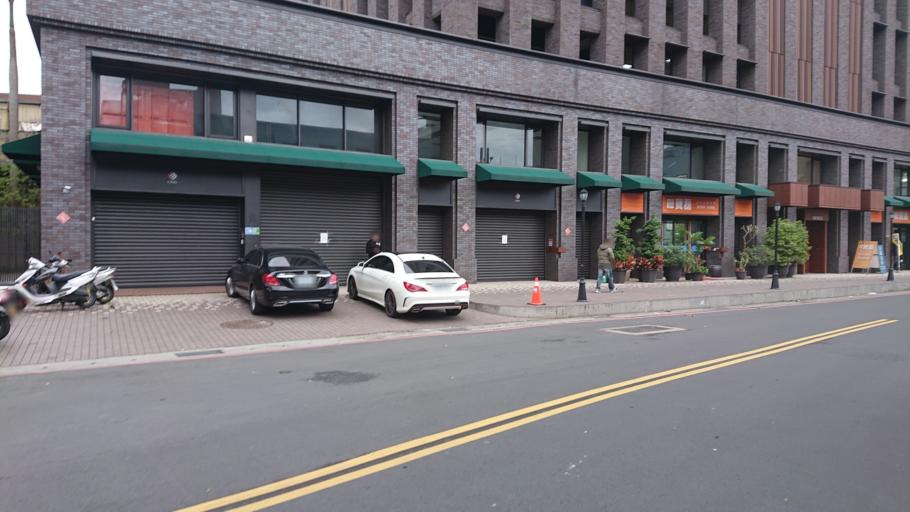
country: TW
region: Taipei
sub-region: Taipei
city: Banqiao
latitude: 24.9649
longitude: 121.4373
